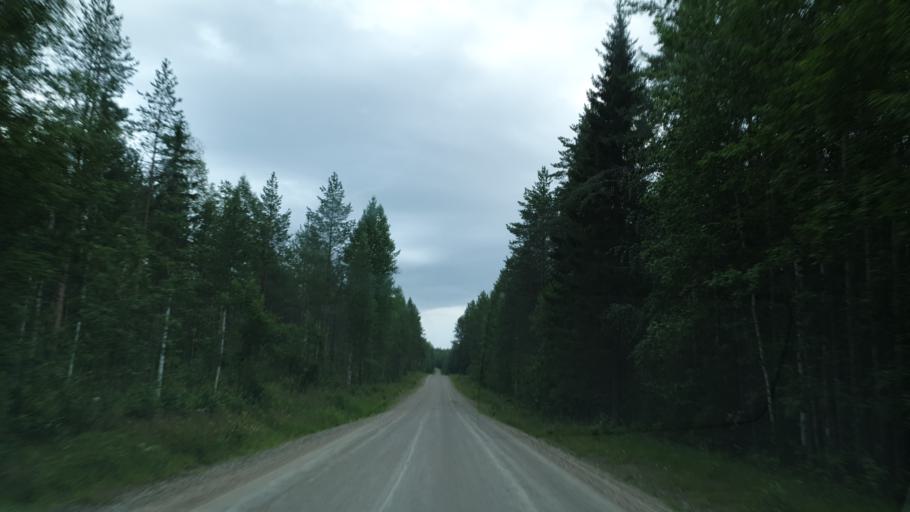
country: FI
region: Kainuu
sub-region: Kehys-Kainuu
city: Kuhmo
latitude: 64.1949
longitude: 29.3689
